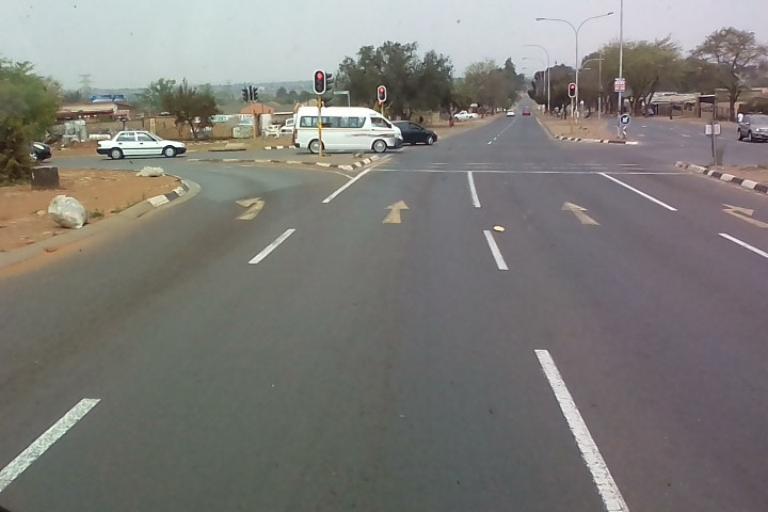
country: ZA
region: Gauteng
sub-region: City of Johannesburg Metropolitan Municipality
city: Soweto
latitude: -26.2347
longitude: 27.8772
